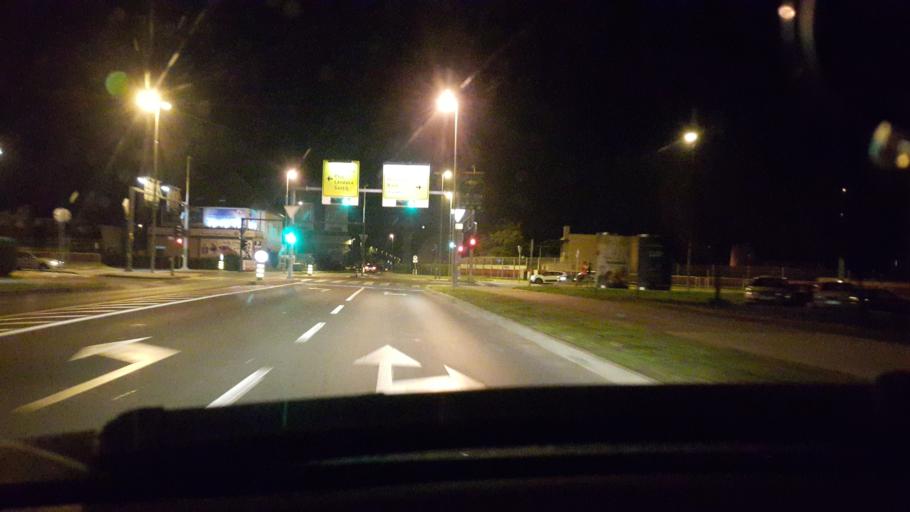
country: SI
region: Maribor
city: Maribor
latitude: 46.5528
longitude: 15.6243
